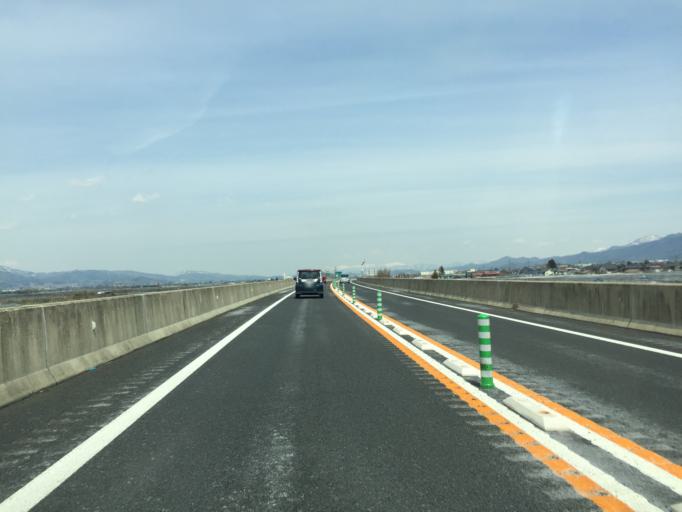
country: JP
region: Yamagata
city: Tendo
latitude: 38.3951
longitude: 140.3426
